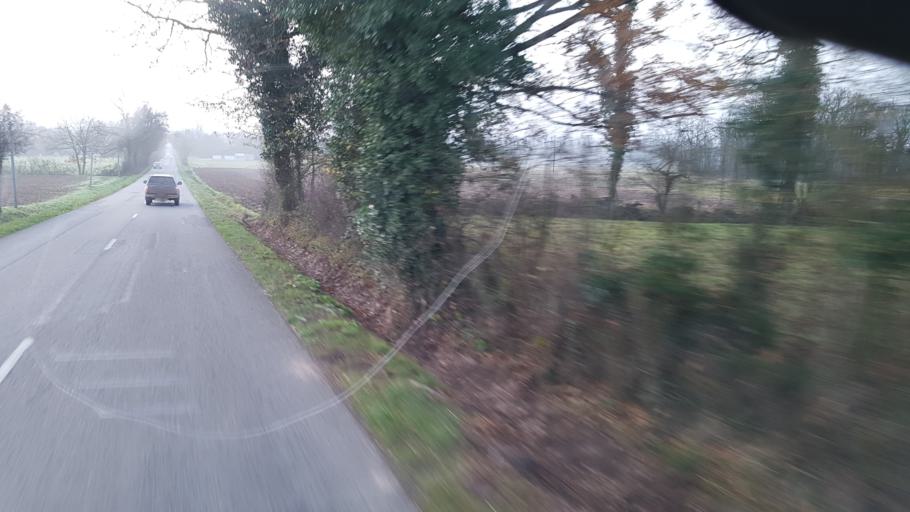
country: FR
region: Midi-Pyrenees
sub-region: Departement du Tarn-et-Garonne
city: Montricoux
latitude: 44.1083
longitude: 1.5959
